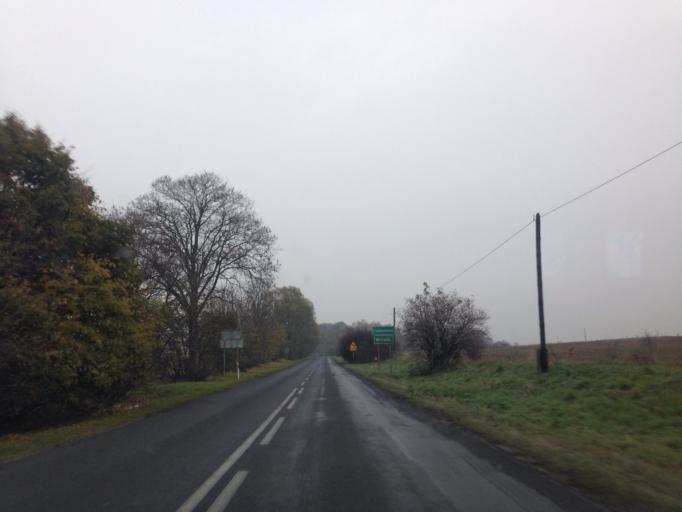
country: PL
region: Kujawsko-Pomorskie
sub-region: Powiat brodnicki
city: Bobrowo
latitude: 53.3109
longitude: 19.2806
